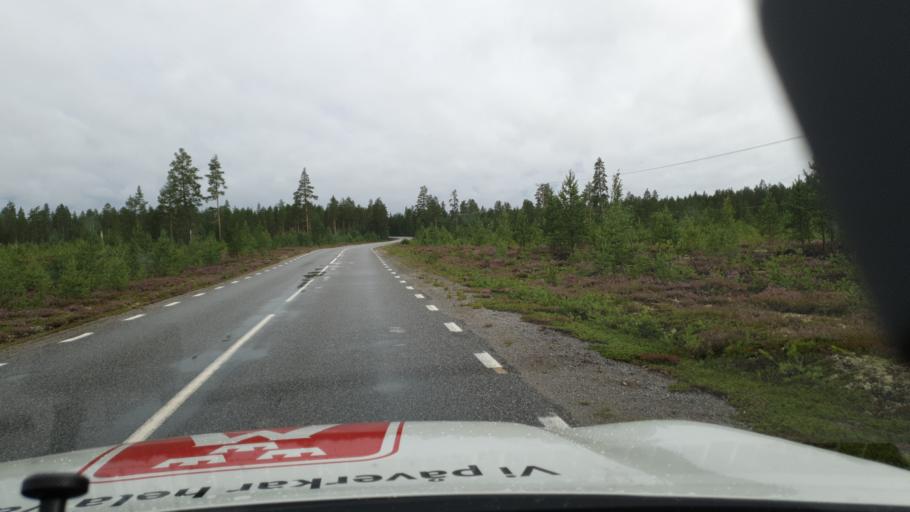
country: SE
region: Vaesterbotten
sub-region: Umea Kommun
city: Saevar
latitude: 63.9833
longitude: 20.5039
